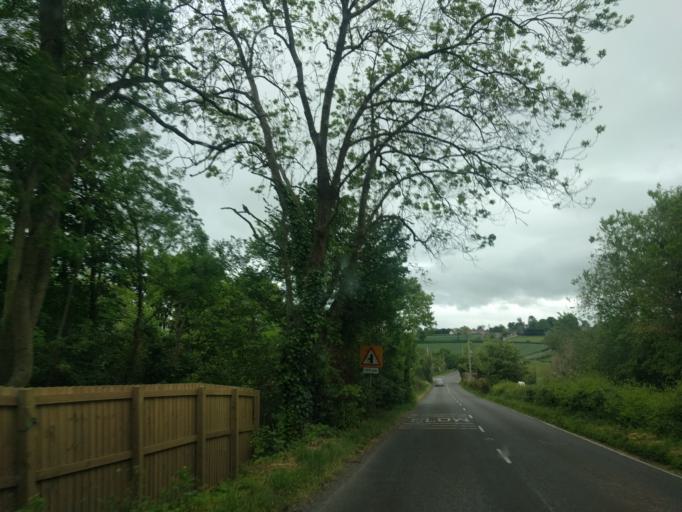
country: GB
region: England
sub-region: Somerset
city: Langport
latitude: 51.0463
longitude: -2.7878
